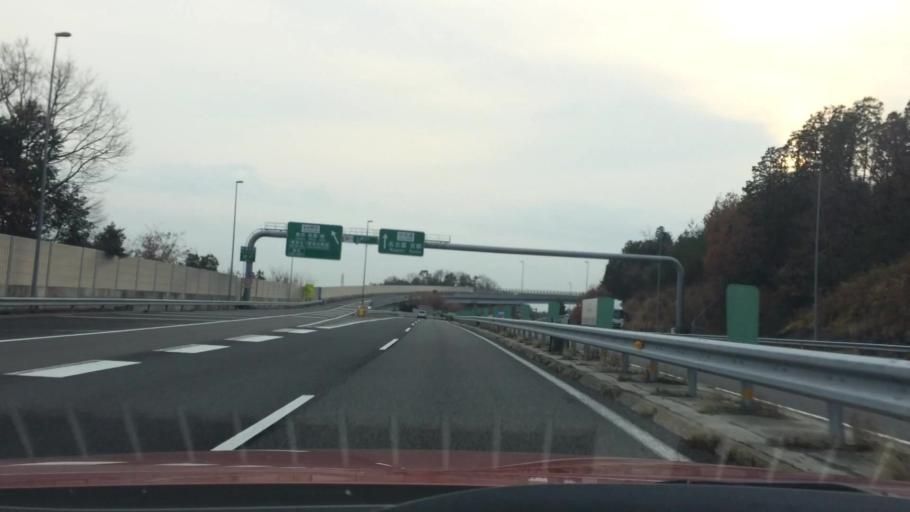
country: JP
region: Gifu
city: Toki
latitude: 35.3655
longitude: 137.1746
